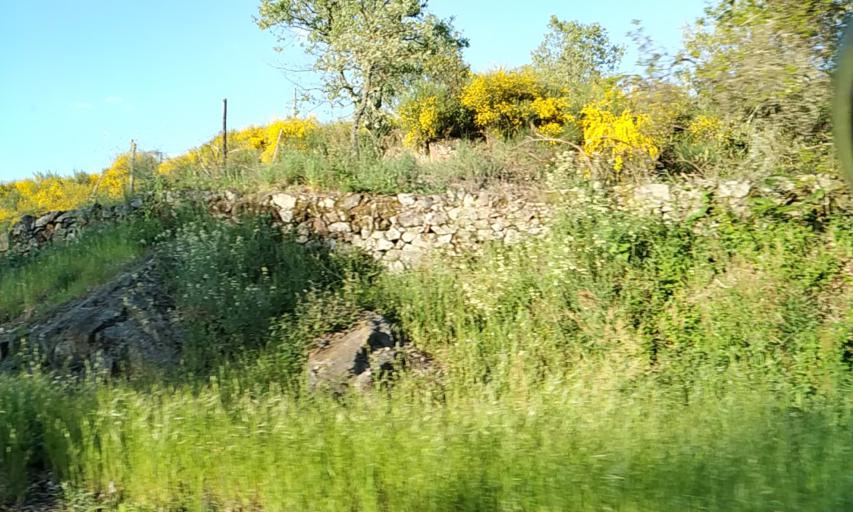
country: PT
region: Portalegre
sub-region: Marvao
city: Marvao
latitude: 39.3634
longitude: -7.4039
